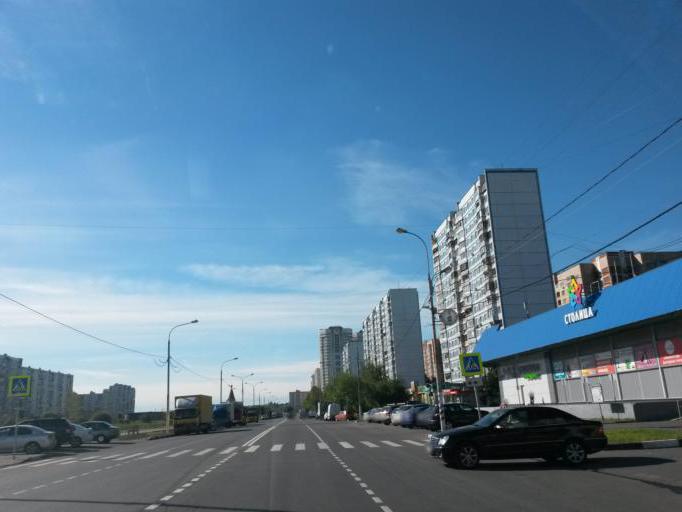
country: RU
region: Moscow
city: Brateyevo
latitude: 55.6384
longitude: 37.7580
